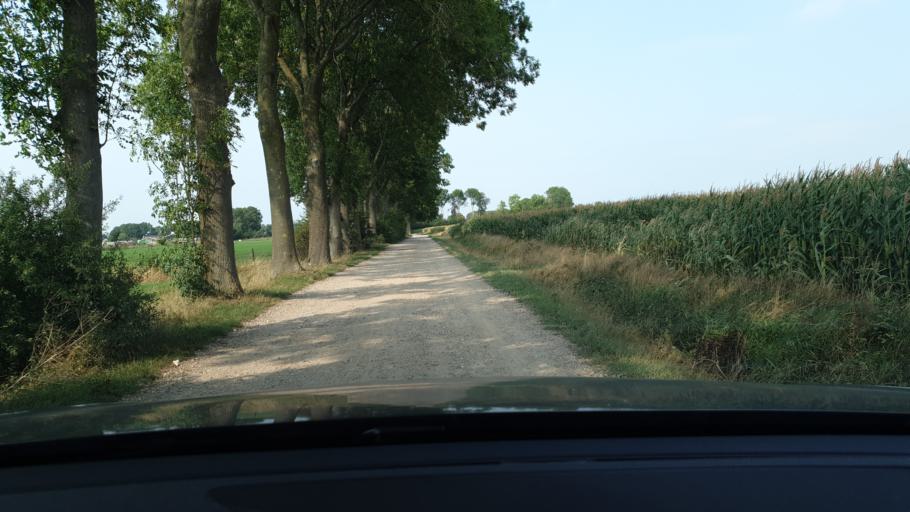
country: NL
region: Gelderland
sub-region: Gemeente Zevenaar
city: Zevenaar
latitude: 51.8537
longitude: 6.0542
